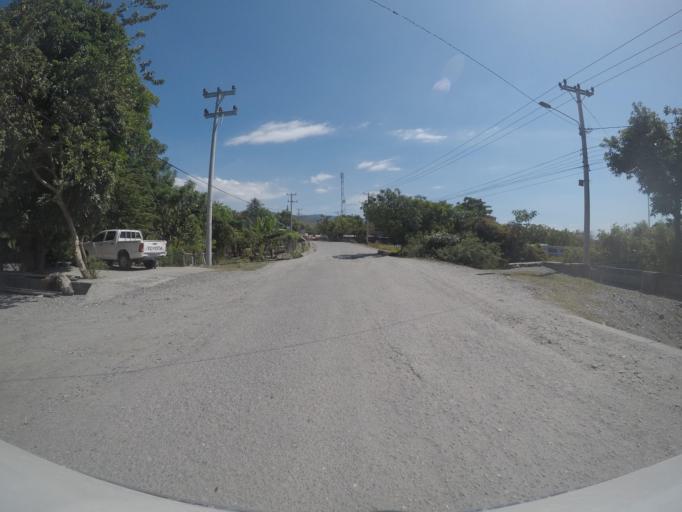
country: TL
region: Liquica
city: Liquica
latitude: -8.5929
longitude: 125.3306
